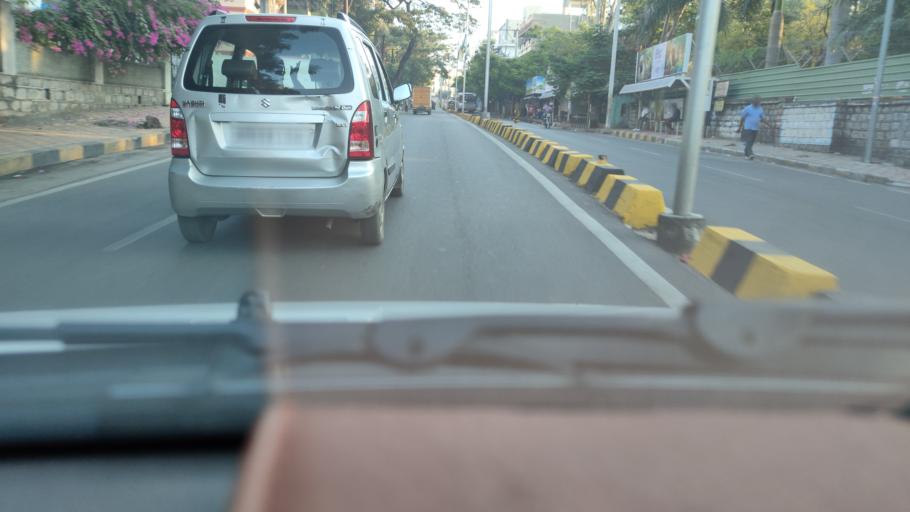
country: IN
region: Telangana
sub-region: Rangareddi
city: Gaddi Annaram
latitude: 17.4030
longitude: 78.5145
